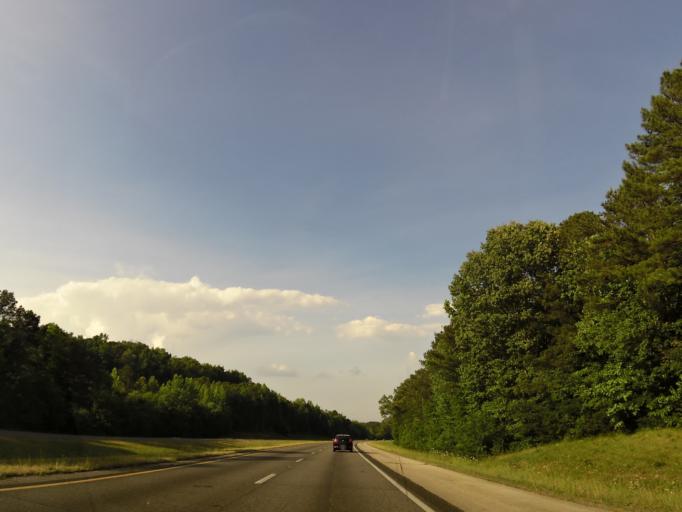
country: US
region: Alabama
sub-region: Jefferson County
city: Argo
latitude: 33.7169
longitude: -86.5159
